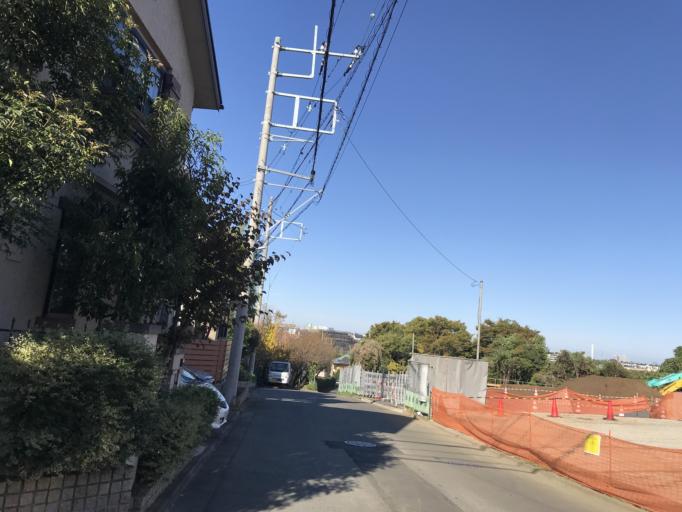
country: JP
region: Tokyo
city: Chofugaoka
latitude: 35.5677
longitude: 139.5892
